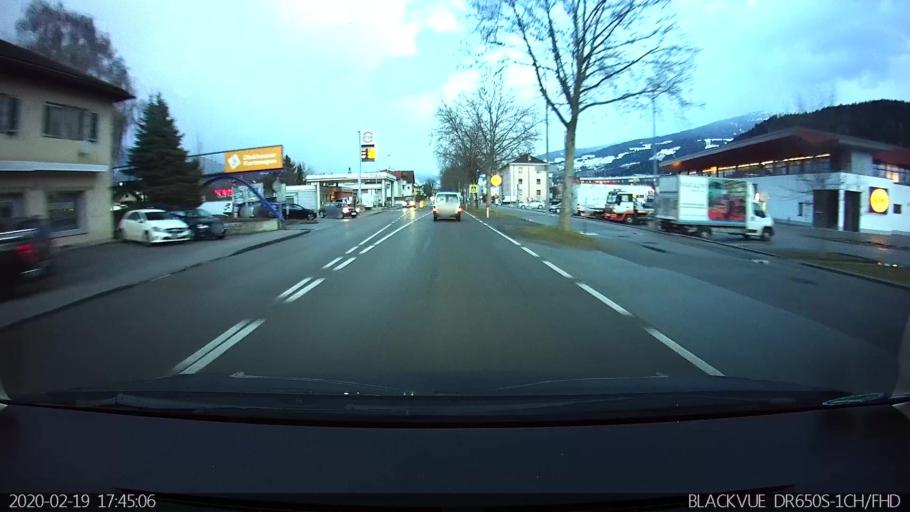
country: AT
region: Tyrol
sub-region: Politischer Bezirk Innsbruck Land
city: Absam
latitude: 47.2779
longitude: 11.4938
